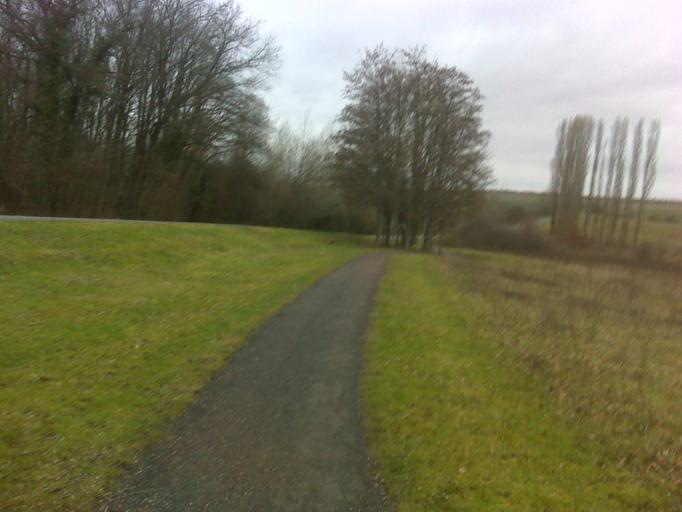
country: FR
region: Lorraine
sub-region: Departement de la Moselle
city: Morhange
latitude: 48.9497
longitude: 6.6334
